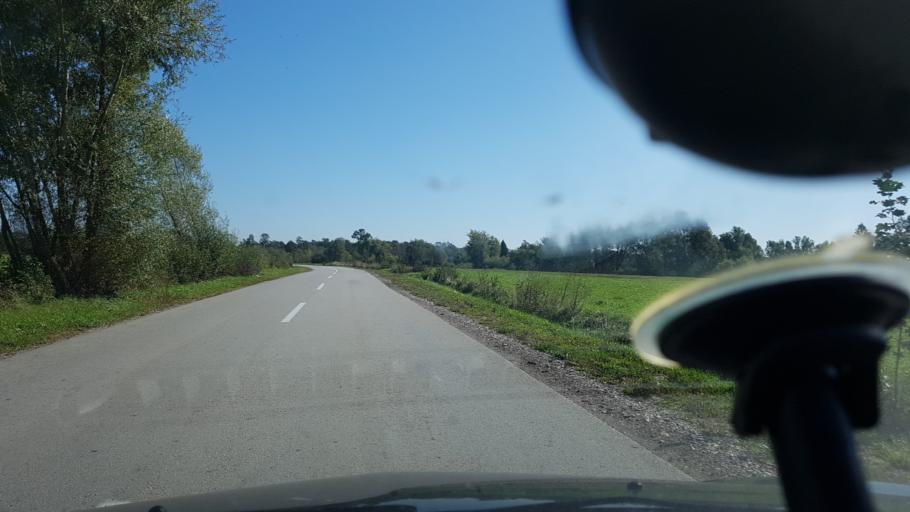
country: HR
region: Zagrebacka
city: Brckovljani
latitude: 45.7597
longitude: 16.2588
